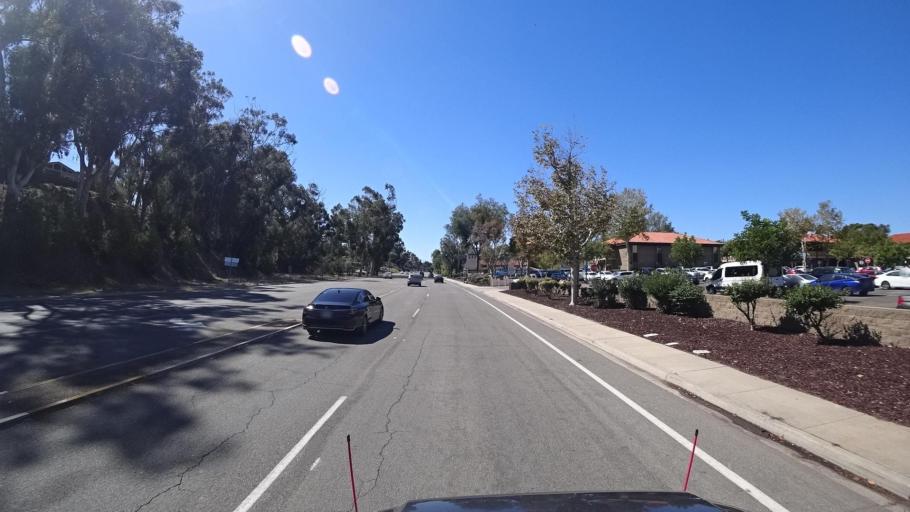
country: US
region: California
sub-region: San Diego County
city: Bonita
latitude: 32.6577
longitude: -117.0415
